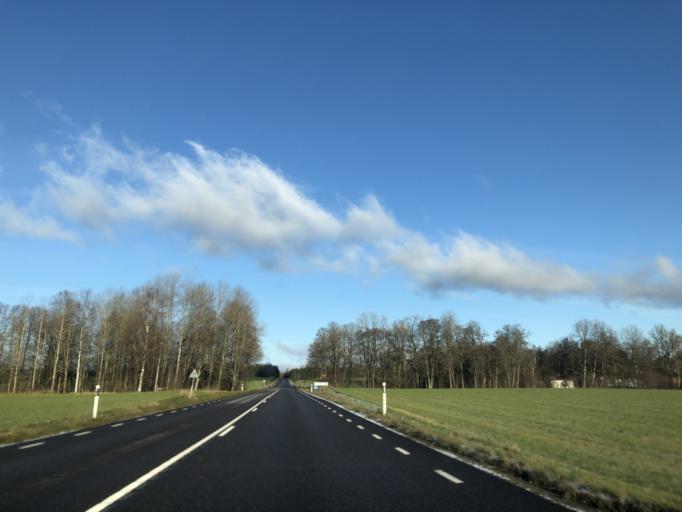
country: SE
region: Vaestra Goetaland
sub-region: Tranemo Kommun
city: Limmared
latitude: 57.6327
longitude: 13.4464
